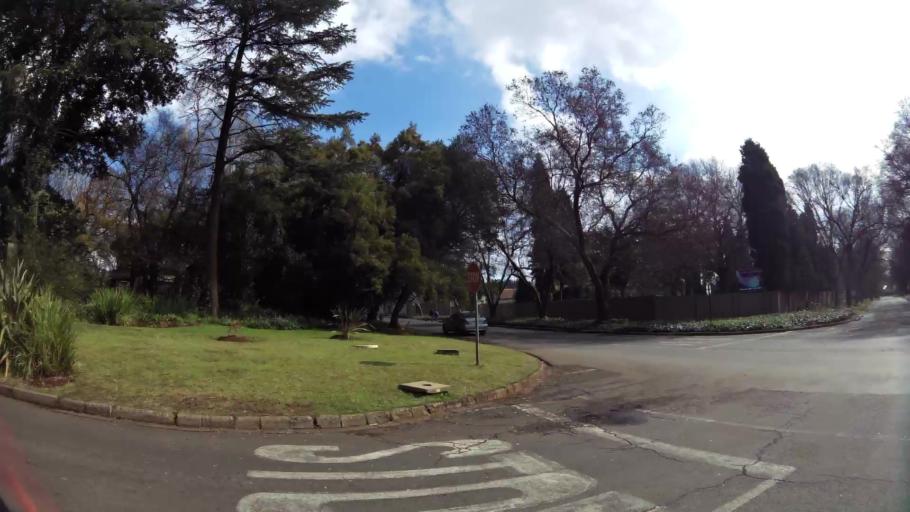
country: ZA
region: Gauteng
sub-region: Sedibeng District Municipality
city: Vanderbijlpark
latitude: -26.7359
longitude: 27.8357
